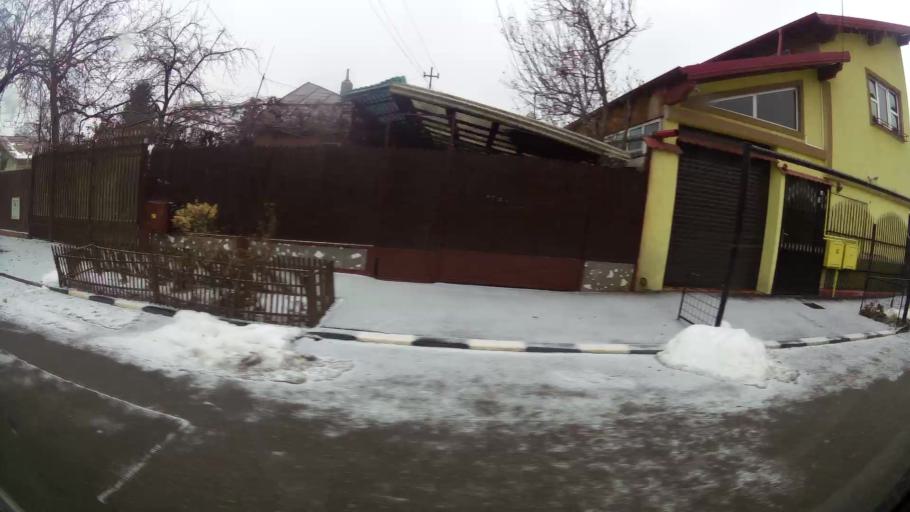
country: RO
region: Prahova
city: Ploiesti
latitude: 44.9541
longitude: 26.0373
